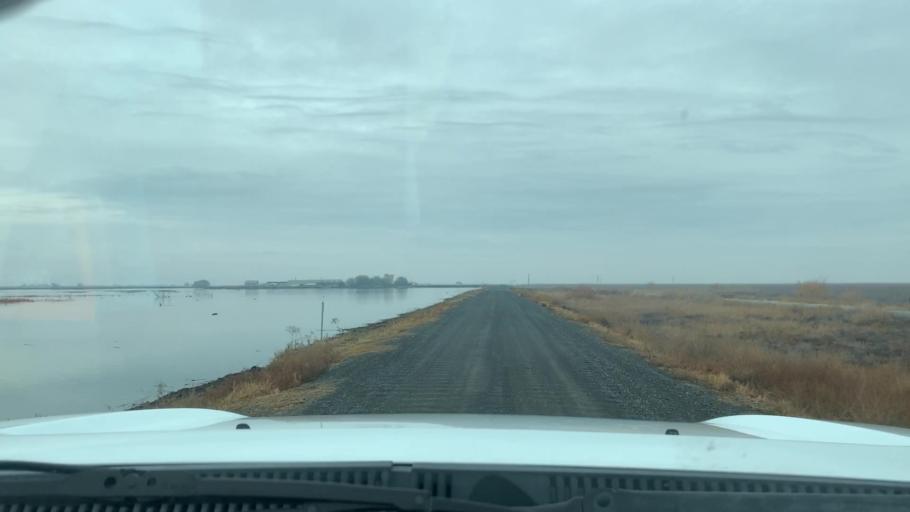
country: US
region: California
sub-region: Tulare County
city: Alpaugh
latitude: 35.7541
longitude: -119.5799
